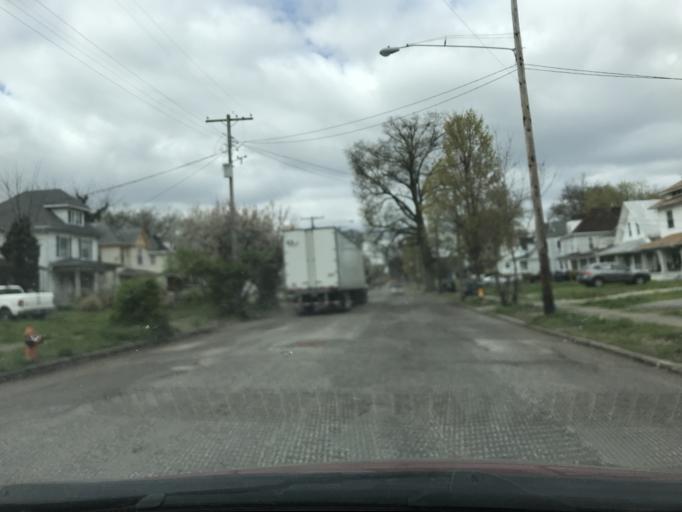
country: US
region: Kentucky
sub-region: Jefferson County
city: Shively
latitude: 38.2385
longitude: -85.8042
